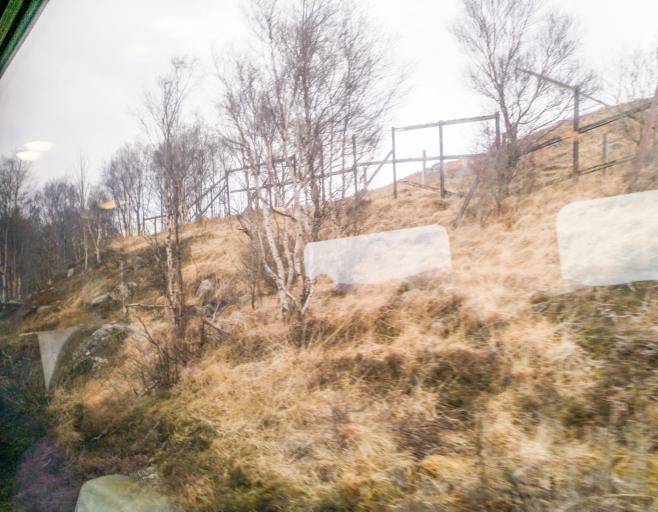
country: GB
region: Scotland
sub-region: Highland
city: Spean Bridge
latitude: 56.7750
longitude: -4.7272
